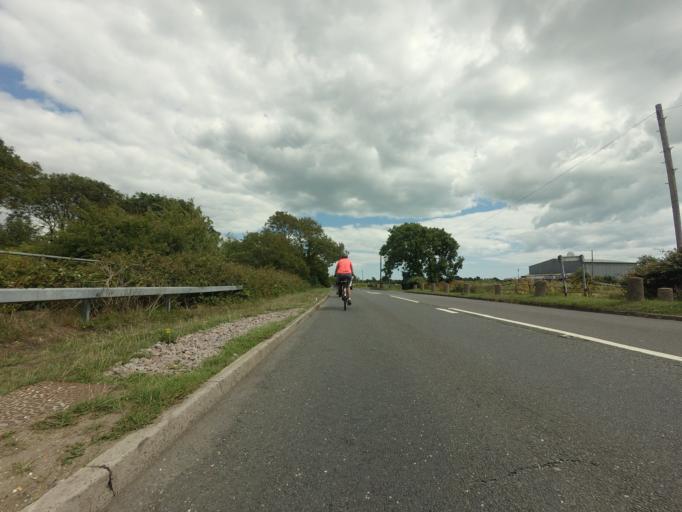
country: GB
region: England
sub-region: East Sussex
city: Pevensey
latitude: 50.8175
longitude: 0.3442
